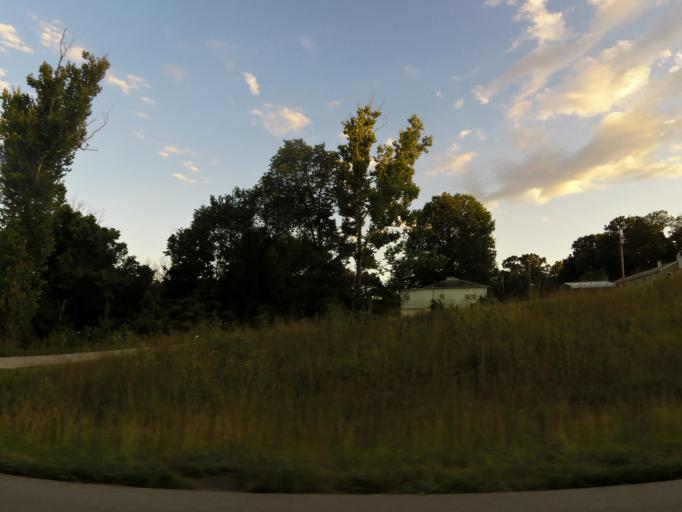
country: US
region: Missouri
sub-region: Jefferson County
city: Cedar Hill
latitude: 38.3405
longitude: -90.6508
